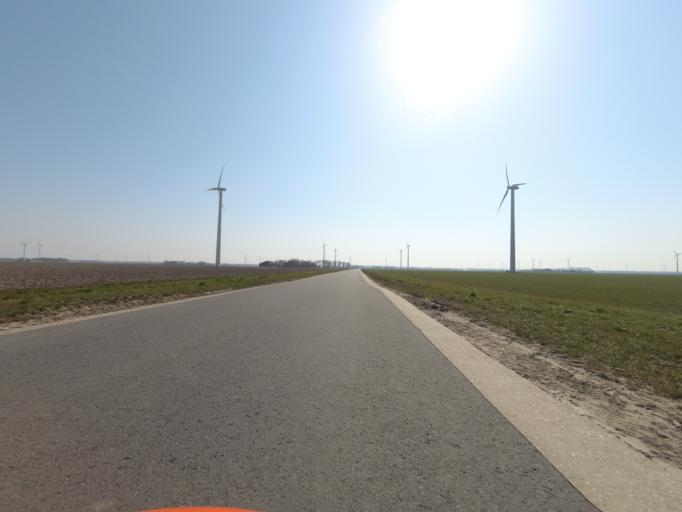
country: NL
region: Utrecht
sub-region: Gemeente Bunschoten
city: Spakenburg
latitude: 52.3405
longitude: 5.3793
